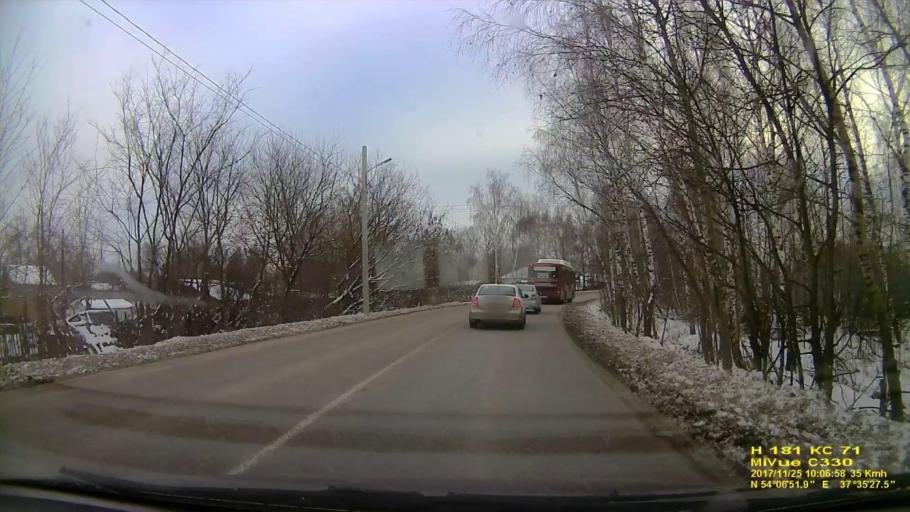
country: RU
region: Tula
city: Skuratovskiy
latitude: 54.1144
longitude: 37.5910
